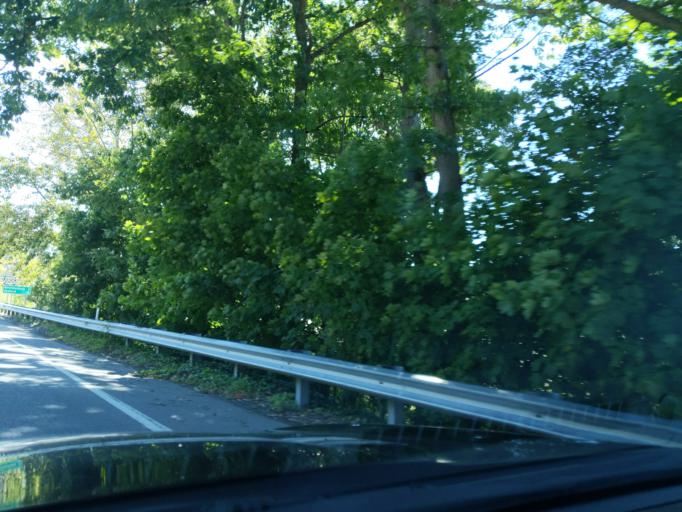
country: US
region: Pennsylvania
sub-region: Blair County
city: Greenwood
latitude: 40.5294
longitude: -78.3633
